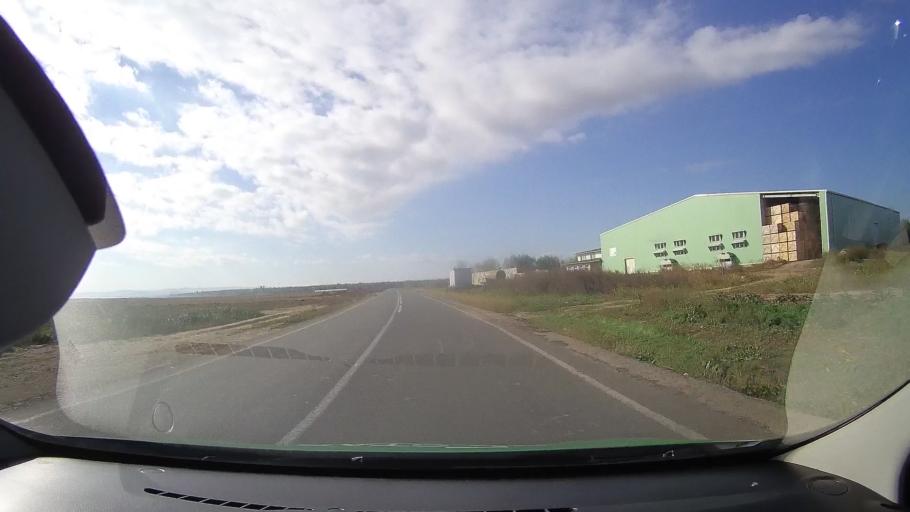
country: RO
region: Tulcea
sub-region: Comuna Sarichioi
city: Sarichioi
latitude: 44.9685
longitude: 28.8684
